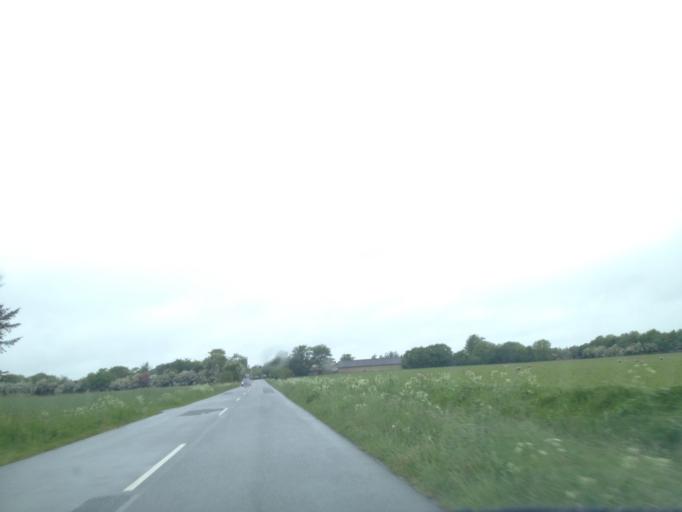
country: DK
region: South Denmark
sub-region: Tonder Kommune
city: Sherrebek
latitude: 55.1192
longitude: 8.7635
